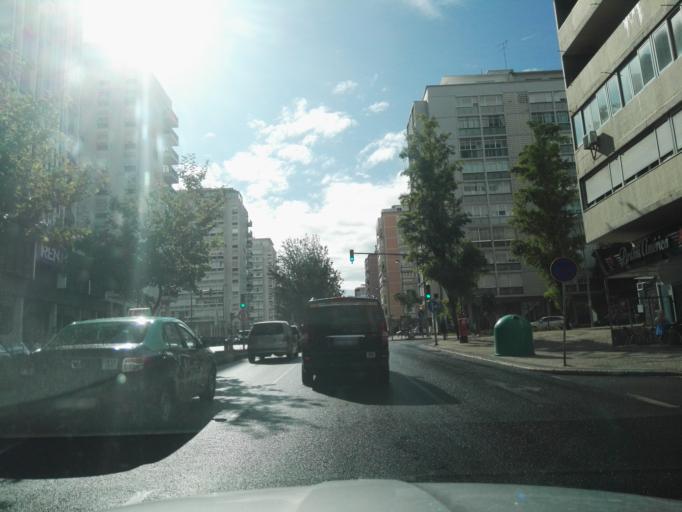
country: PT
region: Lisbon
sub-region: Lisbon
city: Lisbon
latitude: 38.7491
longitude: -9.1370
